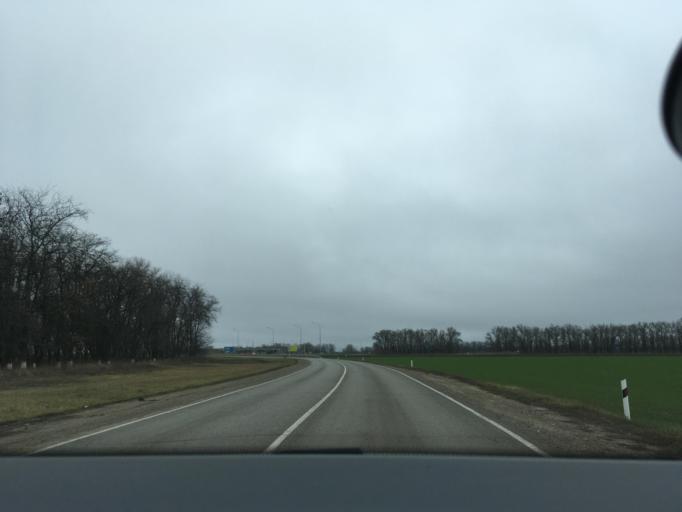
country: RU
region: Krasnodarskiy
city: Kushchevskaya
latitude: 46.6022
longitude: 39.6569
